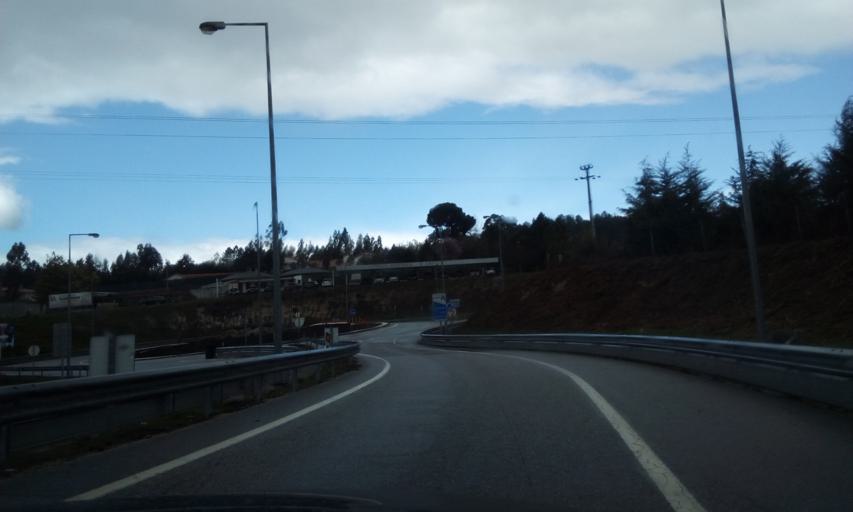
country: PT
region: Viseu
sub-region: Mangualde
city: Mangualde
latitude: 40.6187
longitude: -7.7601
